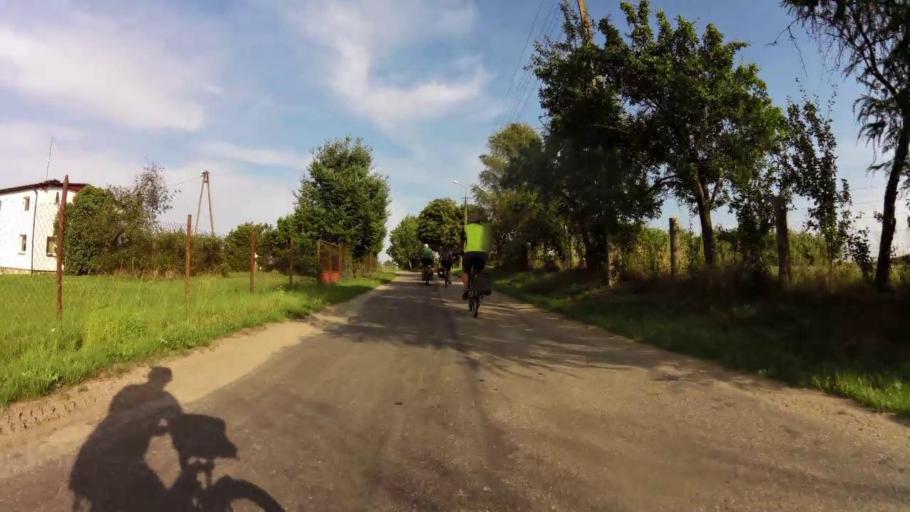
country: PL
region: West Pomeranian Voivodeship
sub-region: Powiat drawski
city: Drawsko Pomorskie
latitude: 53.4922
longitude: 15.7853
